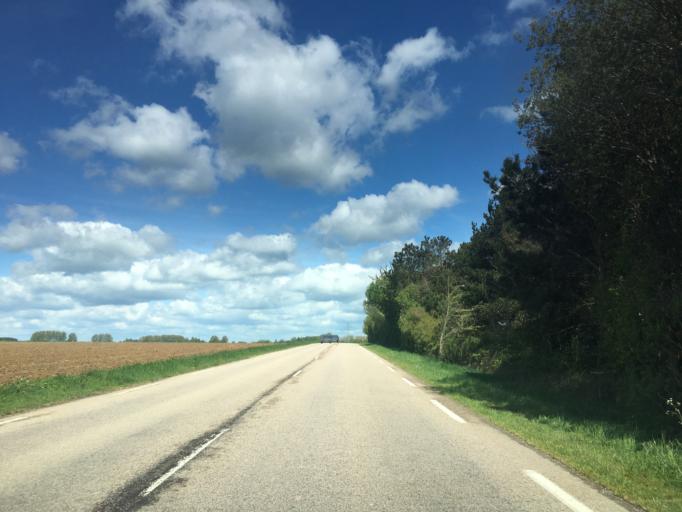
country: FR
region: Lower Normandy
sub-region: Departement de l'Orne
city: Rai
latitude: 48.8082
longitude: 0.5817
